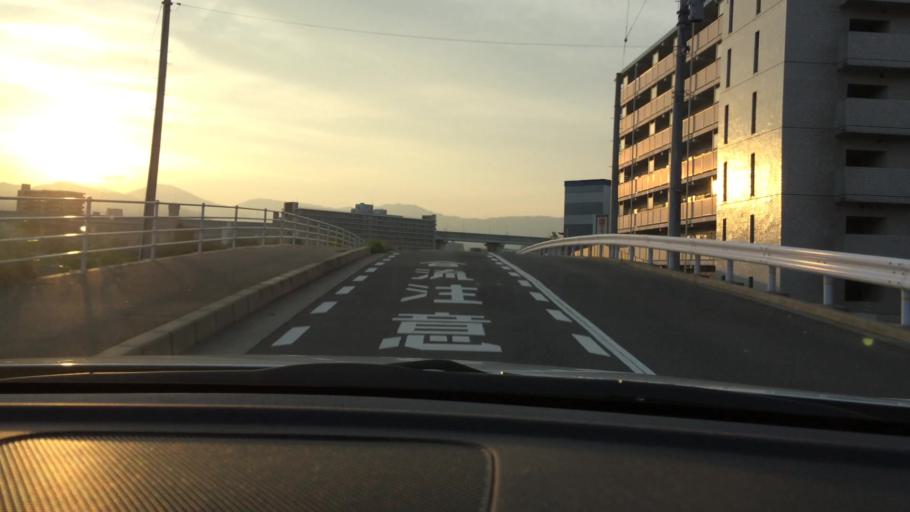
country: JP
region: Hiroshima
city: Hiroshima-shi
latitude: 34.3844
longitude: 132.4928
